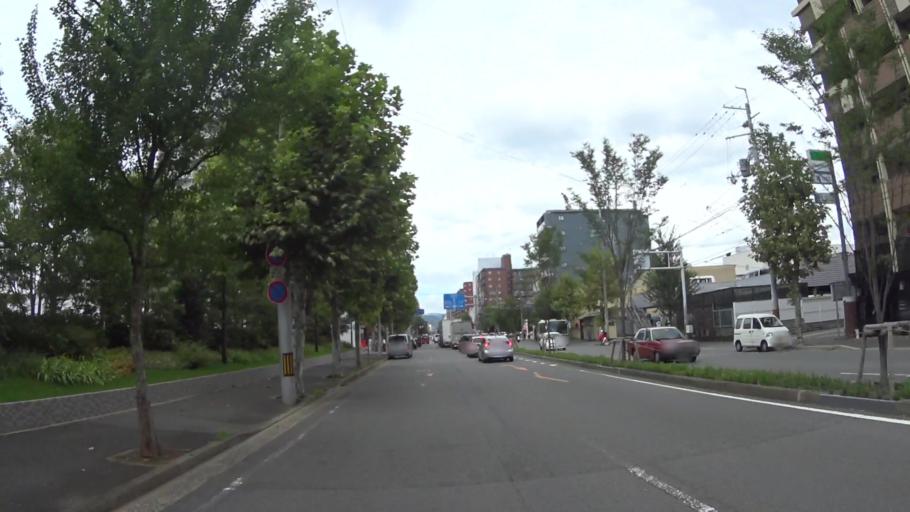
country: JP
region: Kyoto
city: Kyoto
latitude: 34.9947
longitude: 135.7325
